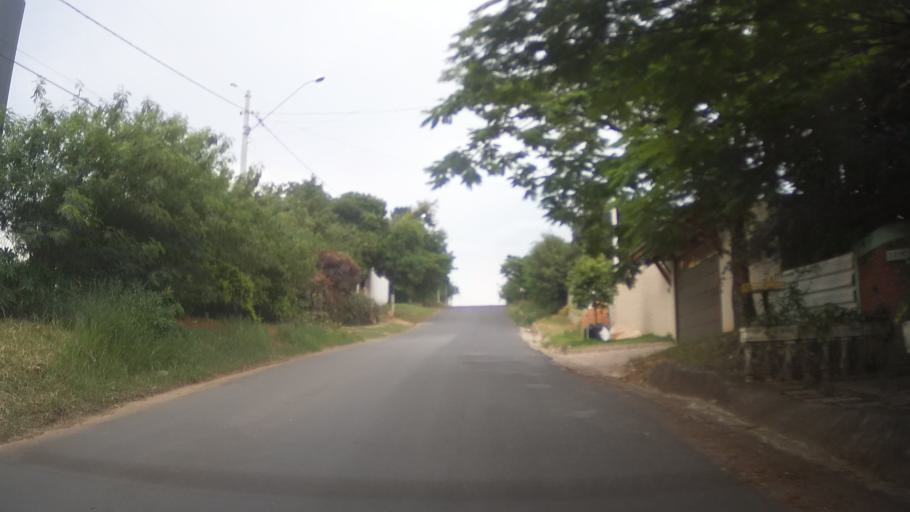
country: BR
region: Sao Paulo
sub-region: Itupeva
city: Itupeva
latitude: -23.1740
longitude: -47.0881
